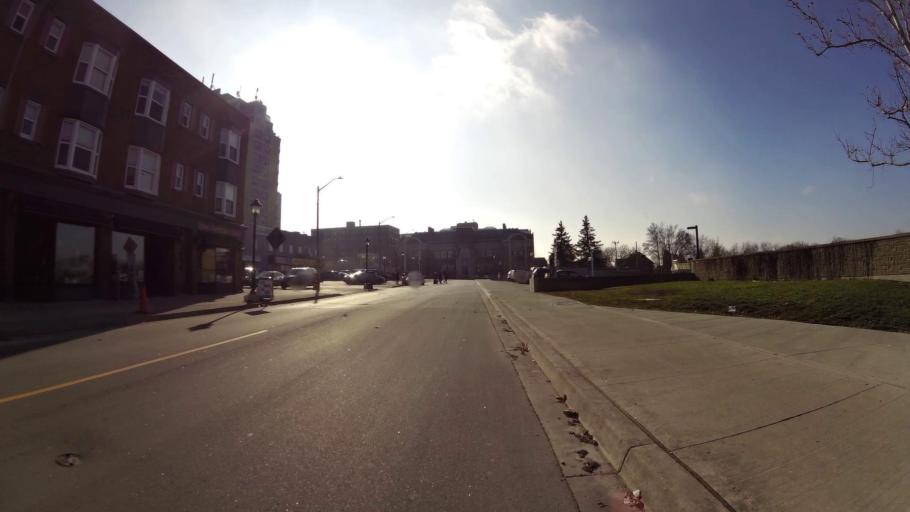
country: CA
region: Ontario
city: Waterloo
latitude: 43.4493
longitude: -80.4913
